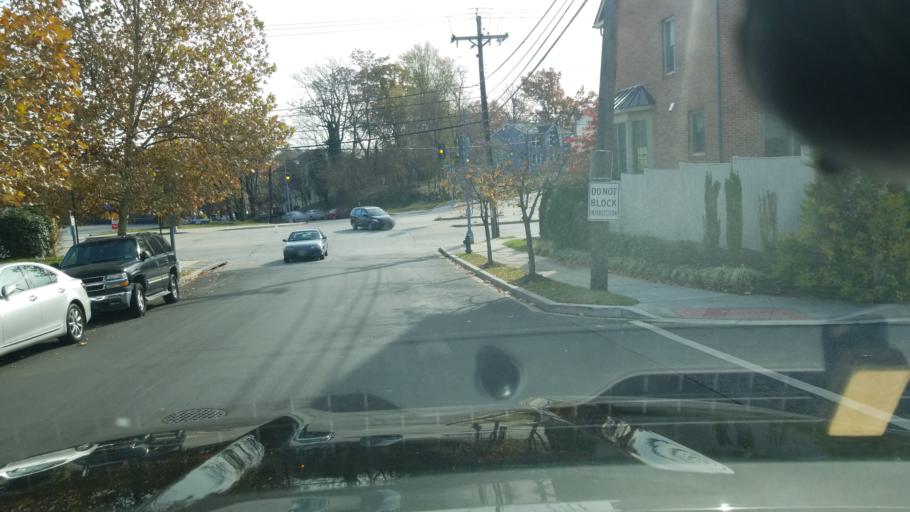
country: US
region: Maryland
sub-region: Prince George's County
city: Chillum
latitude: 38.9654
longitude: -77.0035
